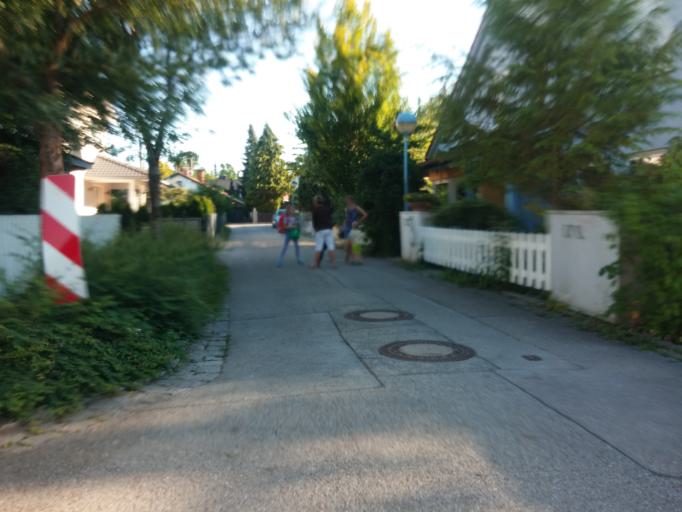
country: DE
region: Bavaria
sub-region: Upper Bavaria
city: Vaterstetten
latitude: 48.1002
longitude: 11.7963
